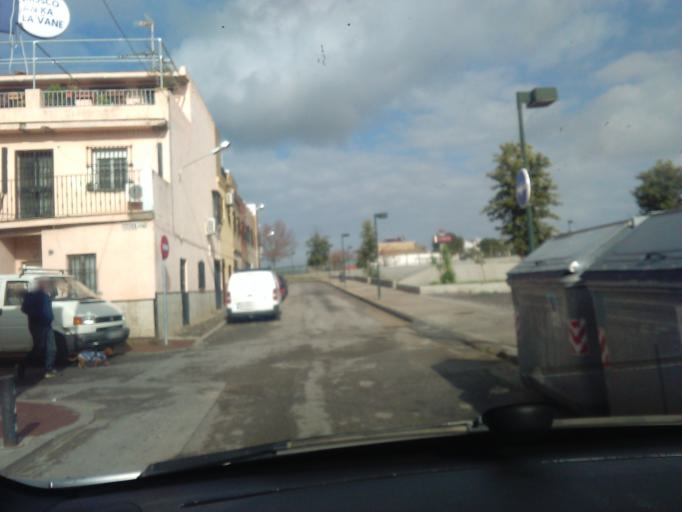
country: ES
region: Andalusia
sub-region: Provincia de Sevilla
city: Sevilla
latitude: 37.3825
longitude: -5.9112
